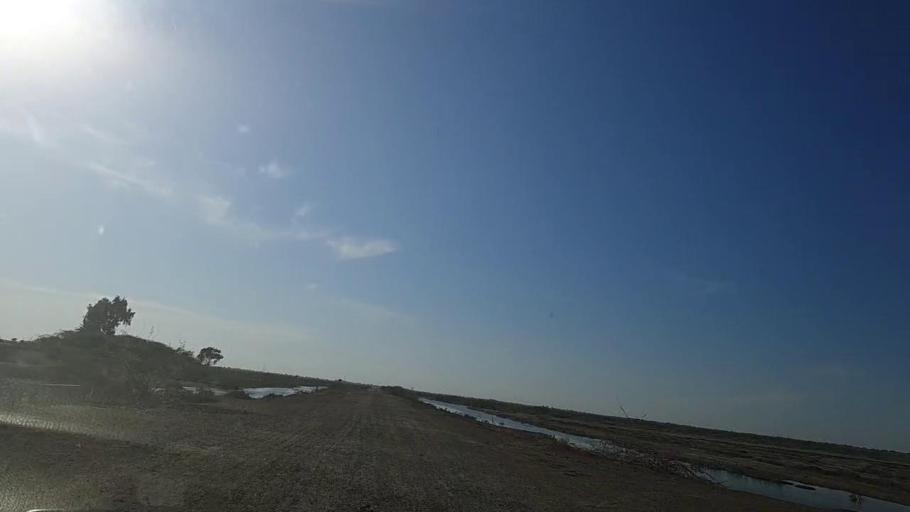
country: PK
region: Sindh
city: Pithoro
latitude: 25.5095
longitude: 69.4307
